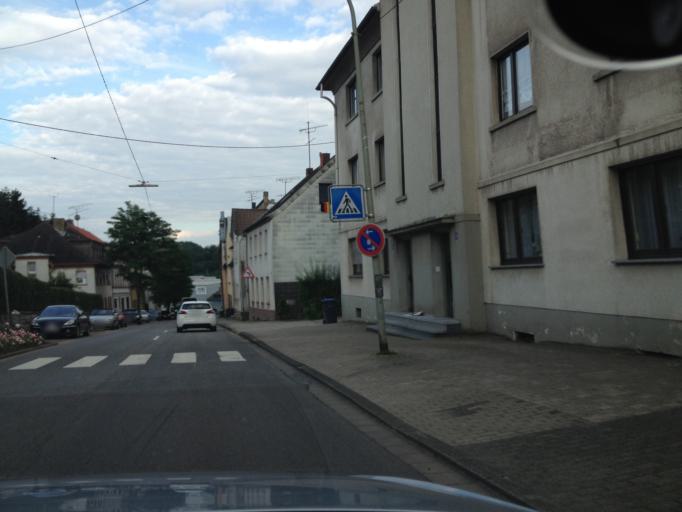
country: DE
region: Saarland
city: Friedrichsthal
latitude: 49.3524
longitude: 7.0973
